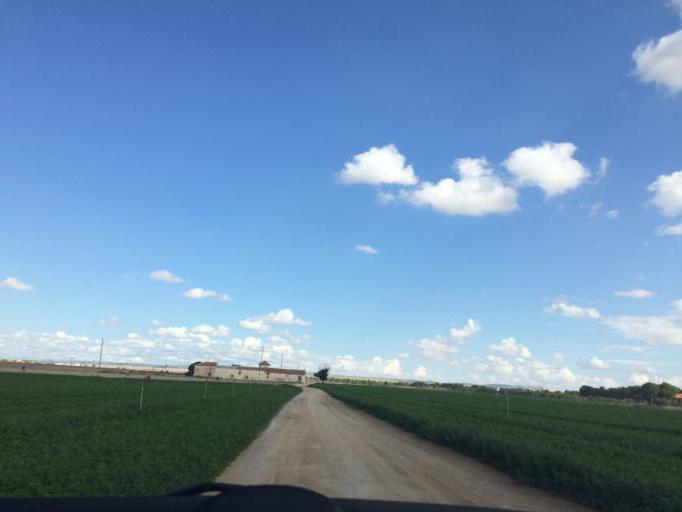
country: ES
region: Castille-La Mancha
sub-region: Provincia de Albacete
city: Albacete
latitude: 38.9587
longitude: -1.8647
